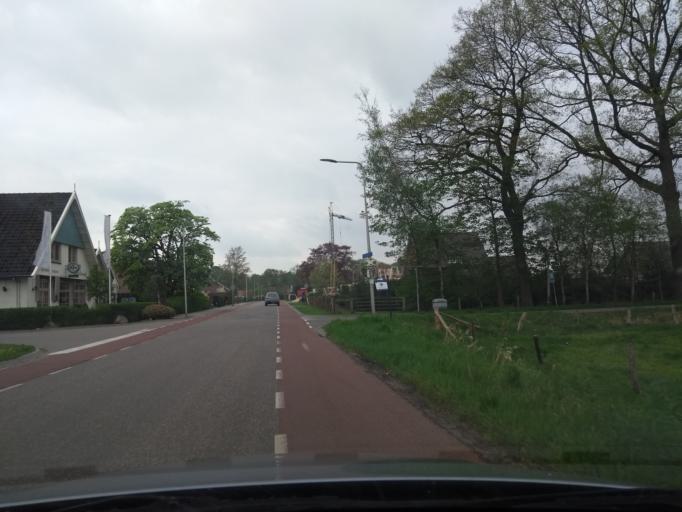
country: DE
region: Lower Saxony
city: Lage
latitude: 52.4183
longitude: 6.9089
